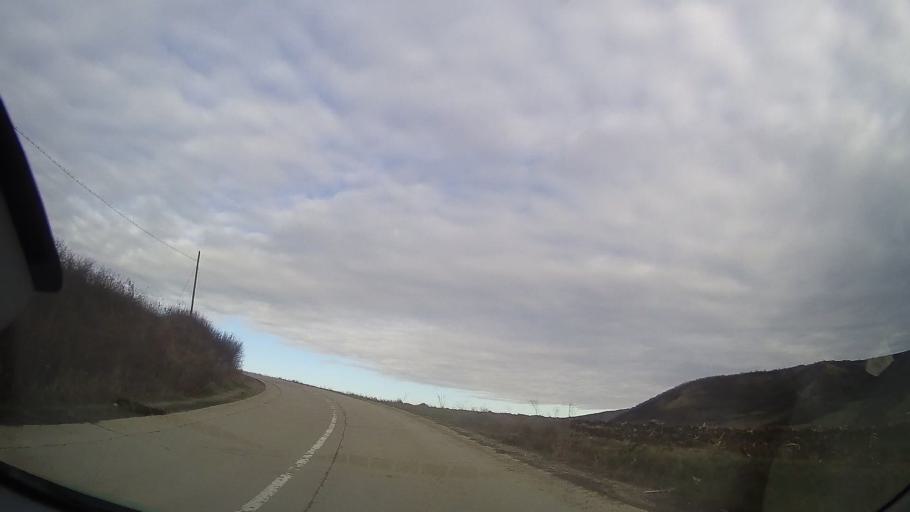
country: RO
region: Bistrita-Nasaud
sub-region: Comuna Sanmihaiu de Campie
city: Sanmihaiu de Campie
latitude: 46.8838
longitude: 24.3329
